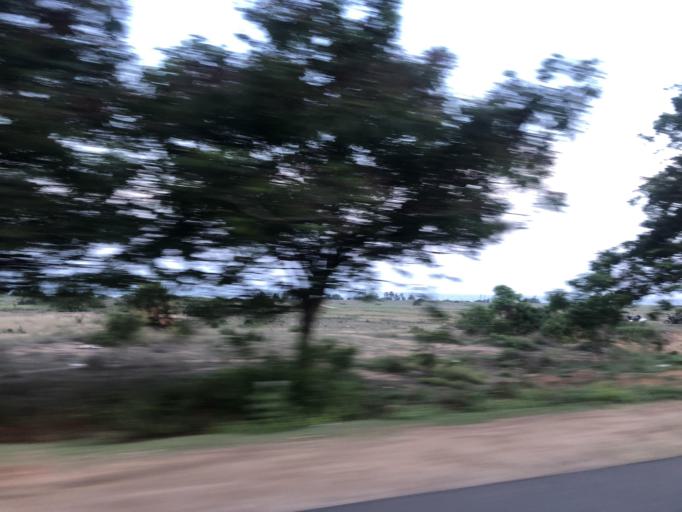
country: IN
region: Tamil Nadu
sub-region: Kancheepuram
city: Mamallapuram
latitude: 12.7544
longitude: 80.2424
